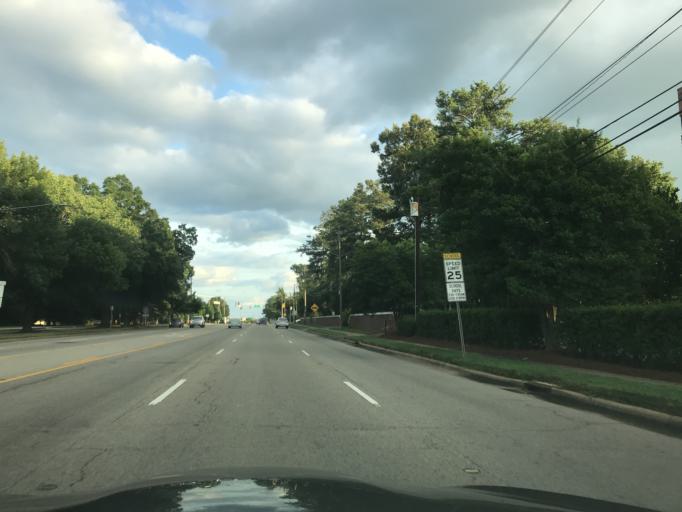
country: US
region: North Carolina
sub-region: Wake County
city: West Raleigh
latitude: 35.8432
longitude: -78.6435
